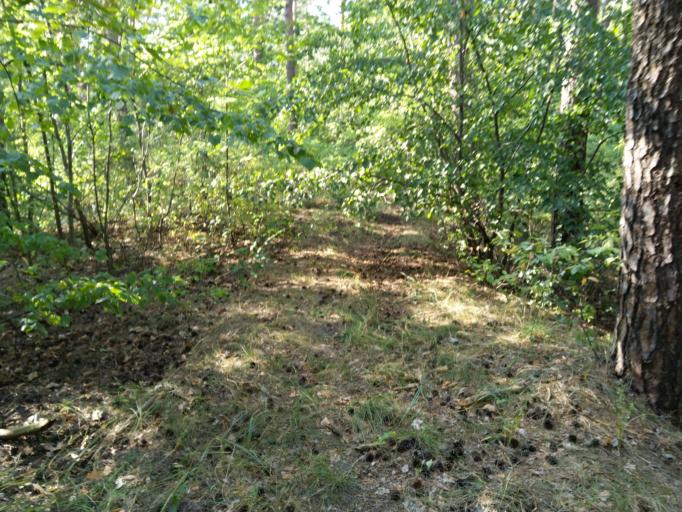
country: DE
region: Brandenburg
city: Woltersdorf
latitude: 52.4487
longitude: 13.7294
